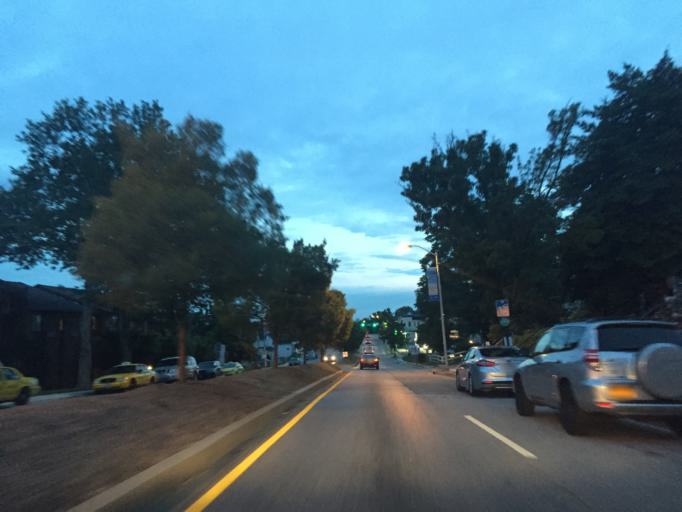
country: US
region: Maryland
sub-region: Baltimore County
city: Parkville
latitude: 39.3485
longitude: -76.5648
